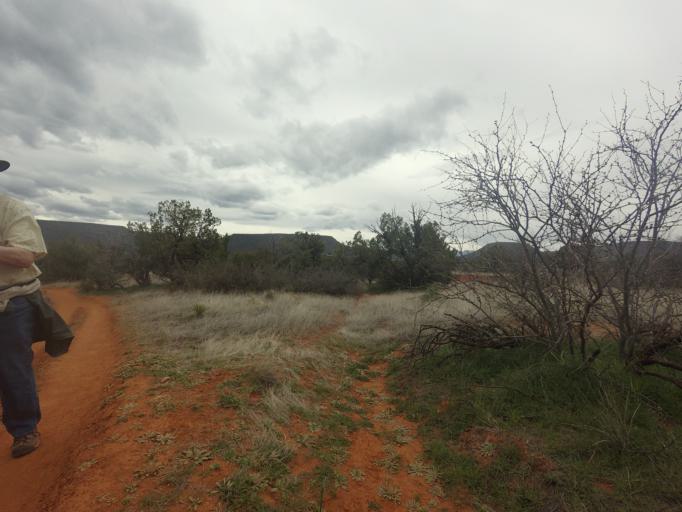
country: US
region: Arizona
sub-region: Yavapai County
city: Village of Oak Creek (Big Park)
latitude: 34.7974
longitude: -111.7569
